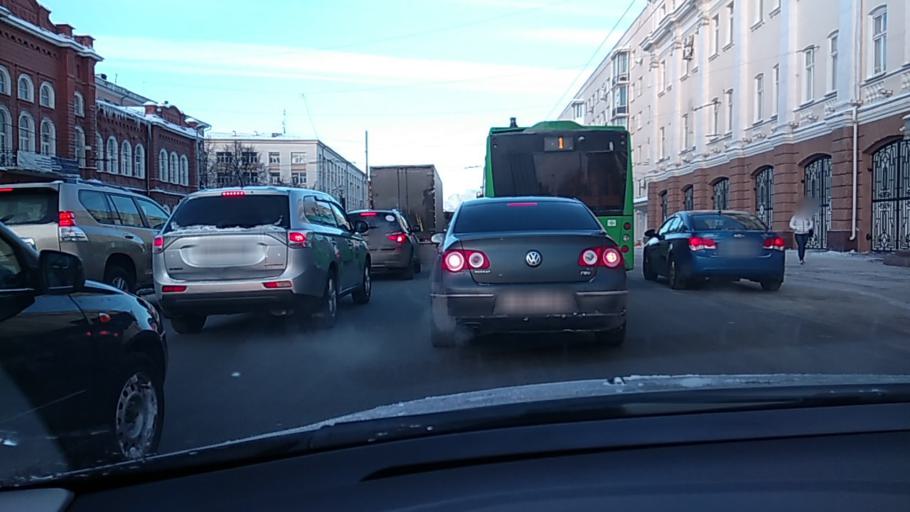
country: RU
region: Sverdlovsk
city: Yekaterinburg
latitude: 56.8370
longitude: 60.6124
